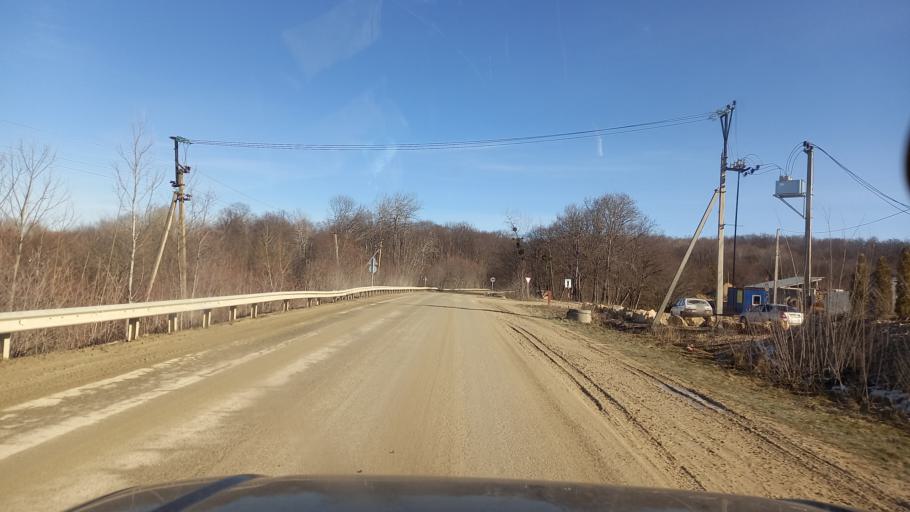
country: RU
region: Adygeya
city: Kamennomostskiy
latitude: 44.2764
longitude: 40.2334
